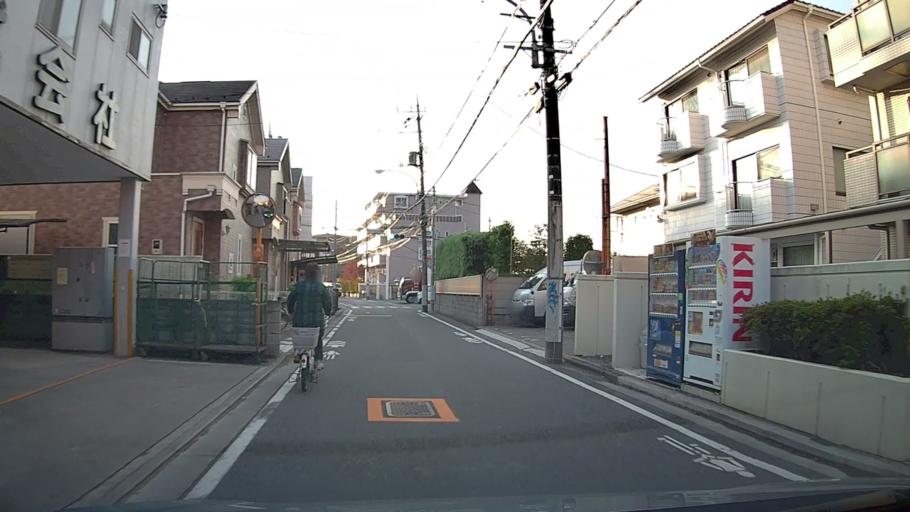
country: JP
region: Saitama
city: Wako
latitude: 35.7513
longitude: 139.6282
